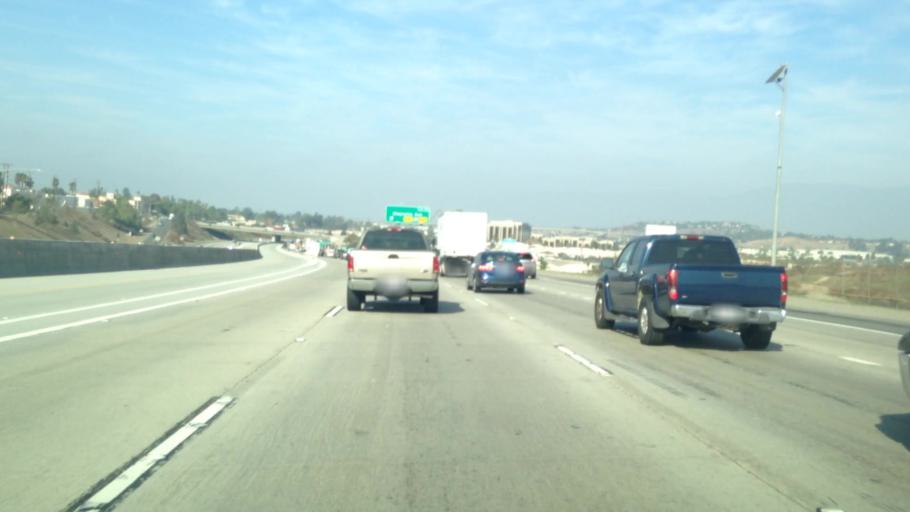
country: US
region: California
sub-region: Riverside County
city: Home Gardens
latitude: 33.8616
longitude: -117.5375
